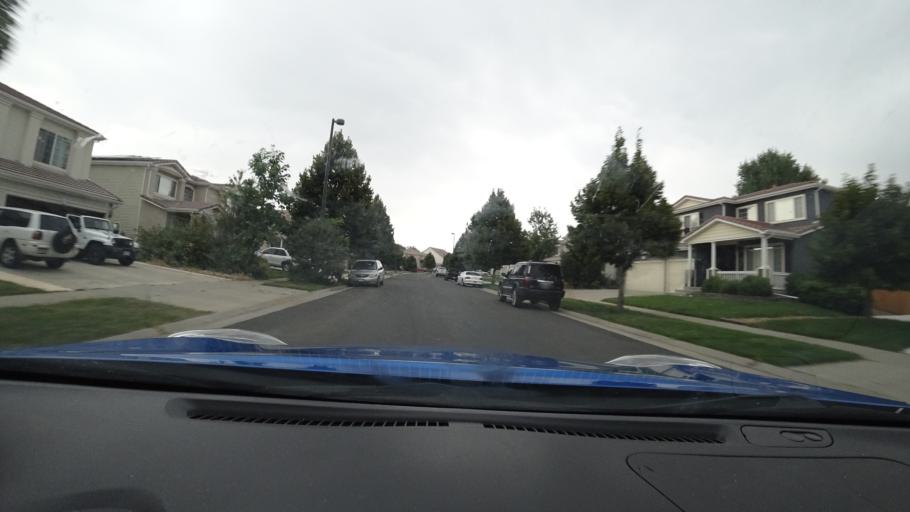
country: US
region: Colorado
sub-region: Adams County
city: Aurora
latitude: 39.7834
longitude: -104.7445
